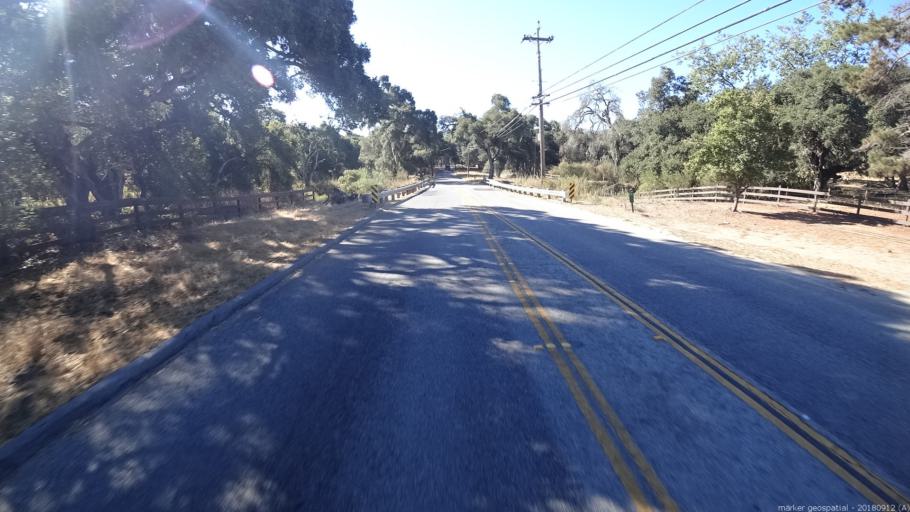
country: US
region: California
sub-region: Monterey County
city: Carmel Valley Village
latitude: 36.5563
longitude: -121.7324
